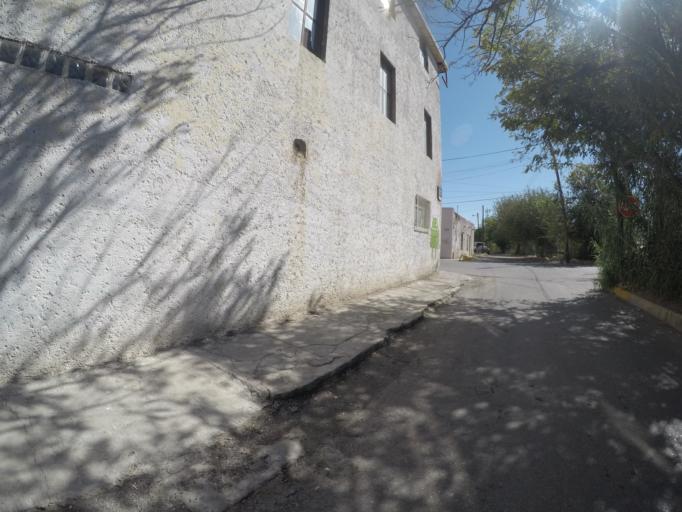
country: MX
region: Chihuahua
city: Ciudad Juarez
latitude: 31.7393
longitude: -106.4775
